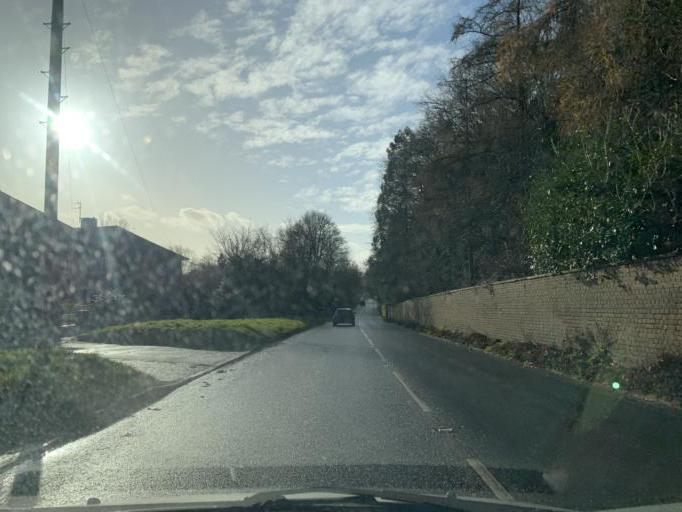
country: GB
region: England
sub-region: Wiltshire
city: Wilton
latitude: 51.0789
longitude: -1.8481
